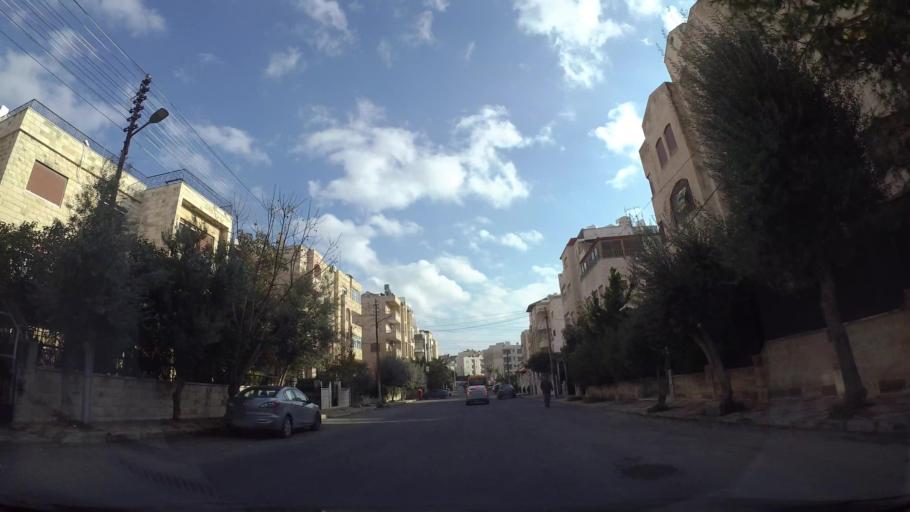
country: JO
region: Amman
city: Al Jubayhah
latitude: 31.9811
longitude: 35.8756
